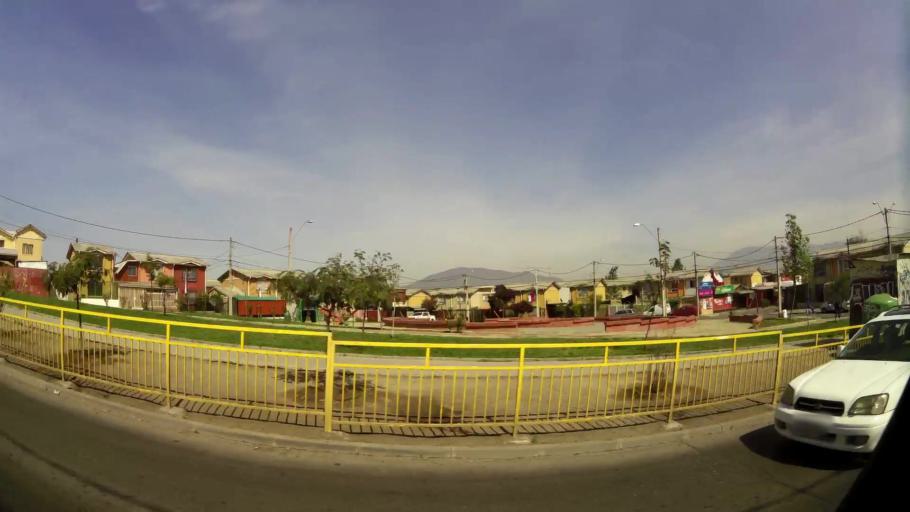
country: CL
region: Santiago Metropolitan
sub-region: Provincia de Santiago
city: Lo Prado
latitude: -33.4388
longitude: -70.7706
